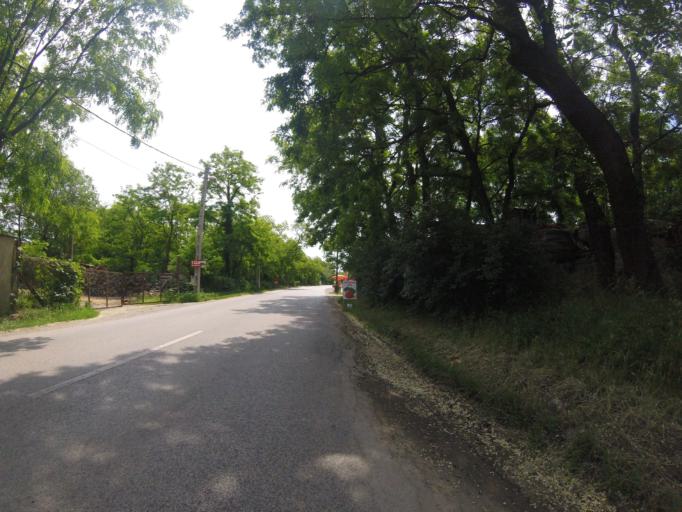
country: HU
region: Pest
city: Tahitotfalu
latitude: 47.7456
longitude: 19.0976
